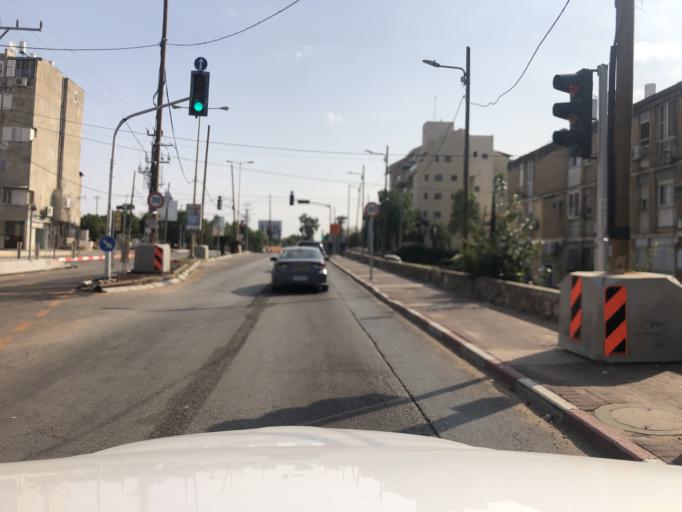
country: IL
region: Central District
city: Kfar Saba
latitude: 32.1724
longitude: 34.9209
